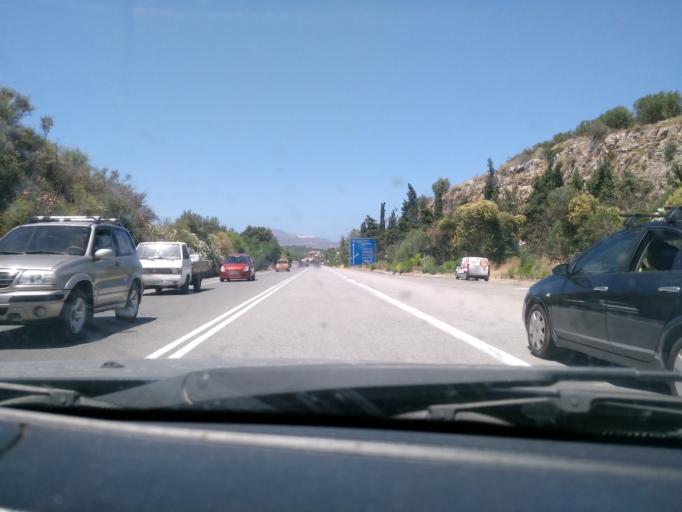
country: GR
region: Crete
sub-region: Nomos Chanias
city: Kalivai
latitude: 35.4339
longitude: 24.1660
